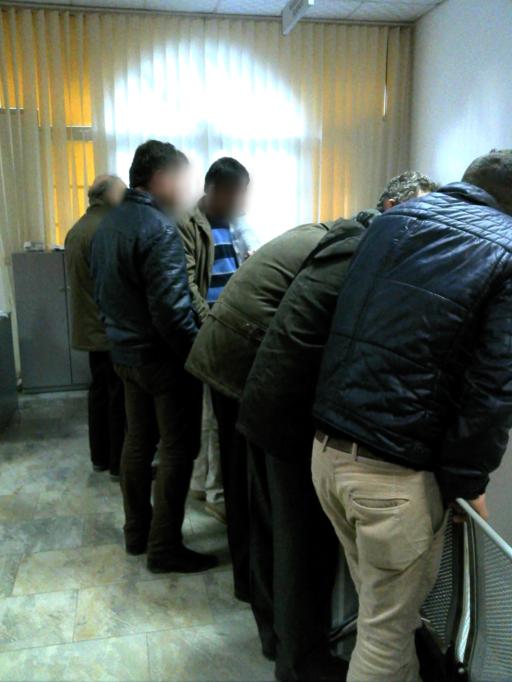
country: AL
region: Shkoder
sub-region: Rrethi i Shkodres
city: Shkoder
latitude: 42.0716
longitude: 19.5200
